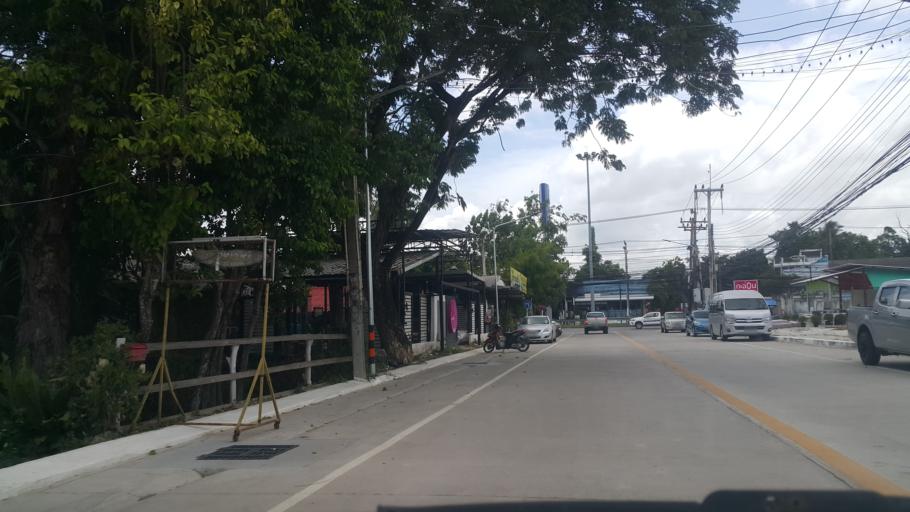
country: TH
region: Rayong
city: Ban Chang
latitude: 12.7279
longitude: 101.0635
